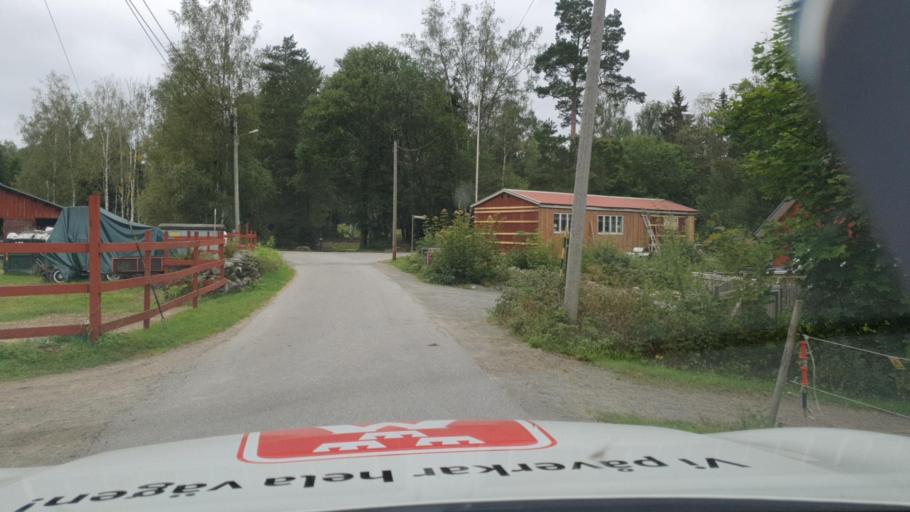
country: SE
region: Vaestra Goetaland
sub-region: Harryda Kommun
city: Hindas
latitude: 57.6987
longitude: 12.4640
